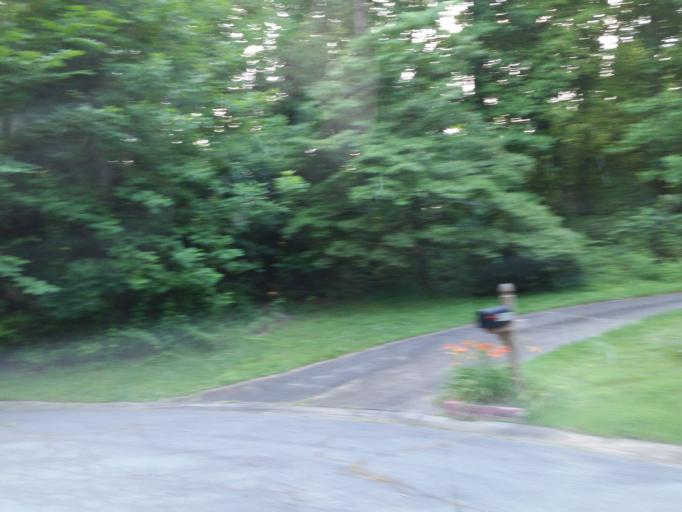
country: US
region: Georgia
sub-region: Cherokee County
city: Woodstock
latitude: 34.0671
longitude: -84.4916
